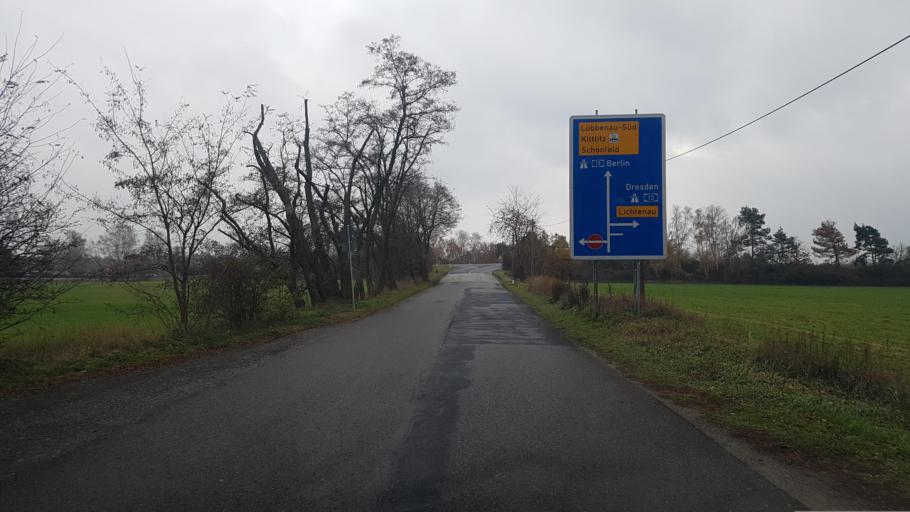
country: DE
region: Brandenburg
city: Lubbenau
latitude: 51.8331
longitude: 13.9094
